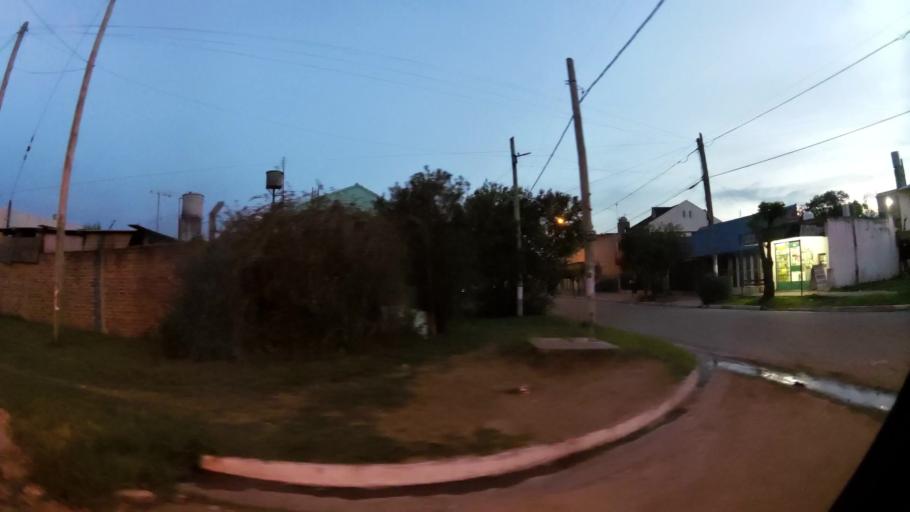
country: AR
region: Buenos Aires
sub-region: Partido de Almirante Brown
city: Adrogue
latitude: -34.8051
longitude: -58.2942
